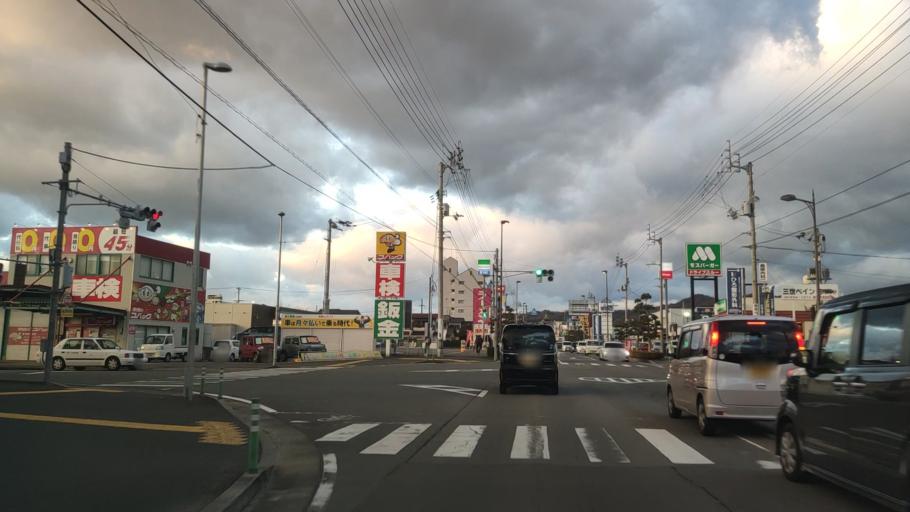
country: JP
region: Ehime
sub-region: Shikoku-chuo Shi
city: Matsuyama
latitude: 33.8327
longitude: 132.7872
